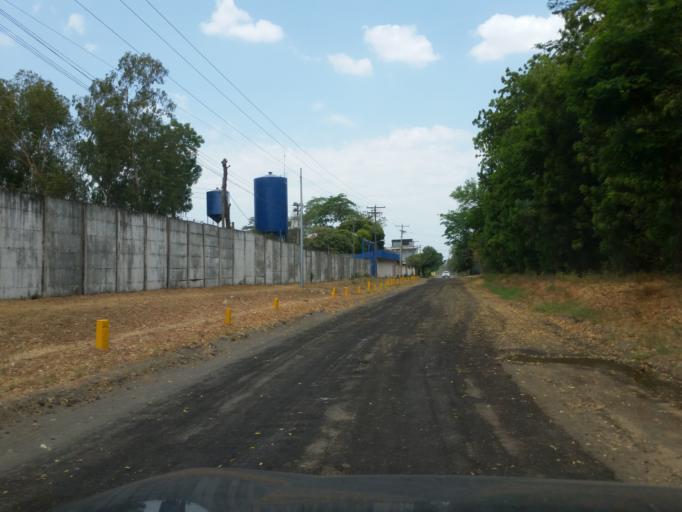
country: NI
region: Managua
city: Managua
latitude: 12.1284
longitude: -86.1647
